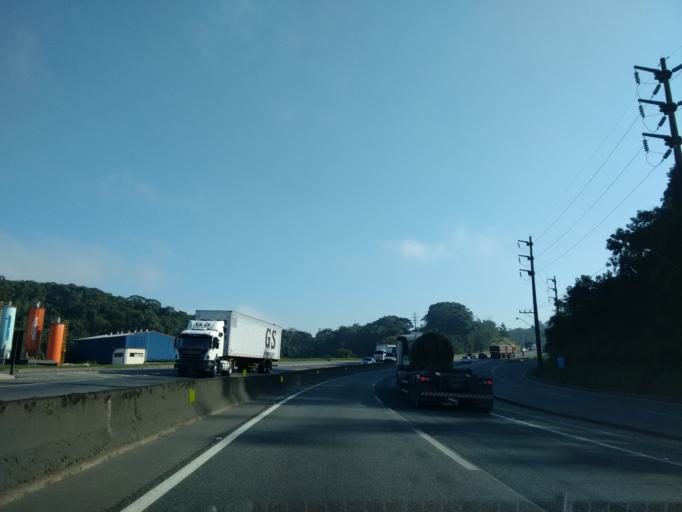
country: BR
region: Santa Catarina
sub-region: Joinville
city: Joinville
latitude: -26.3168
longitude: -48.8733
